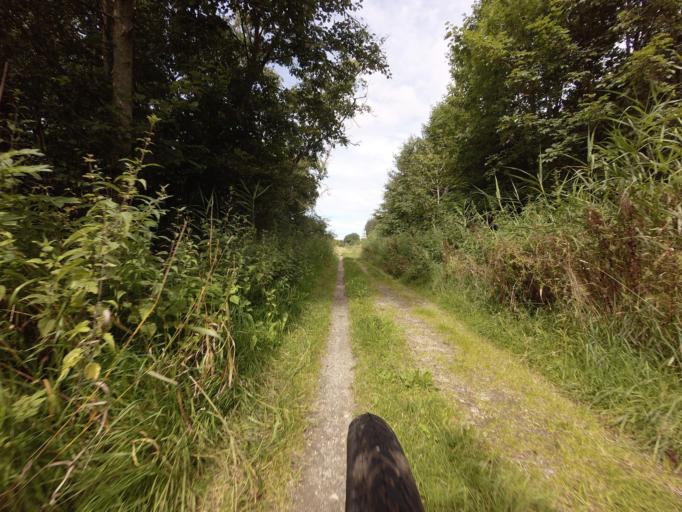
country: DK
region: Central Jutland
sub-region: Syddjurs Kommune
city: Ryomgard
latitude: 56.3886
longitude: 10.5327
